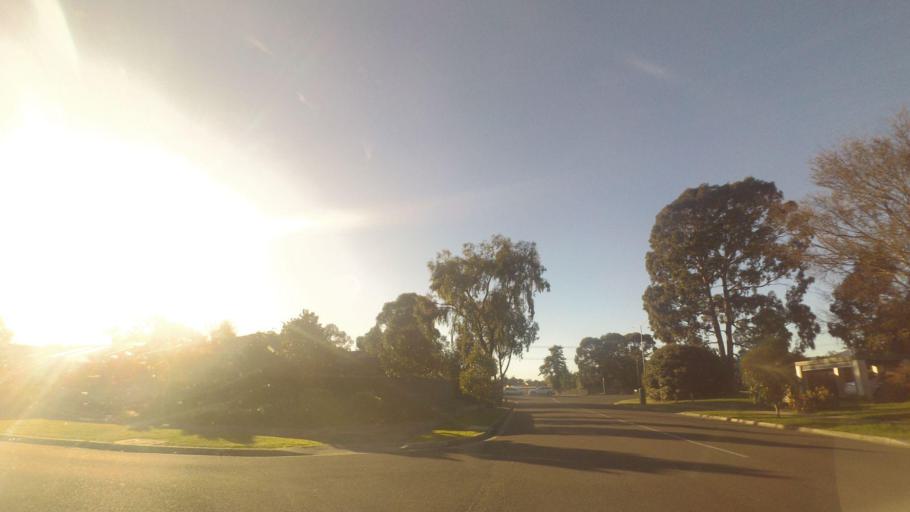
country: AU
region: Victoria
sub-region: Knox
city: Knoxfield
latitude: -37.9146
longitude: 145.2632
